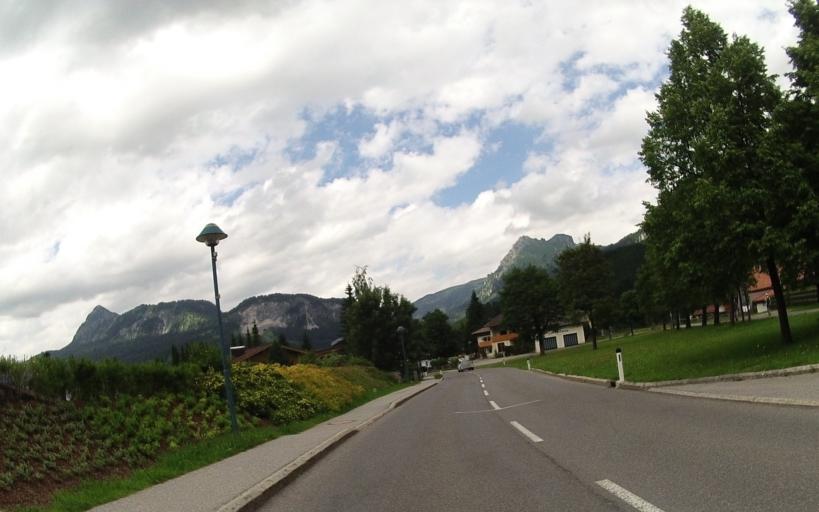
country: AT
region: Tyrol
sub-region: Politischer Bezirk Reutte
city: Graen
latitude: 47.4933
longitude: 10.5602
